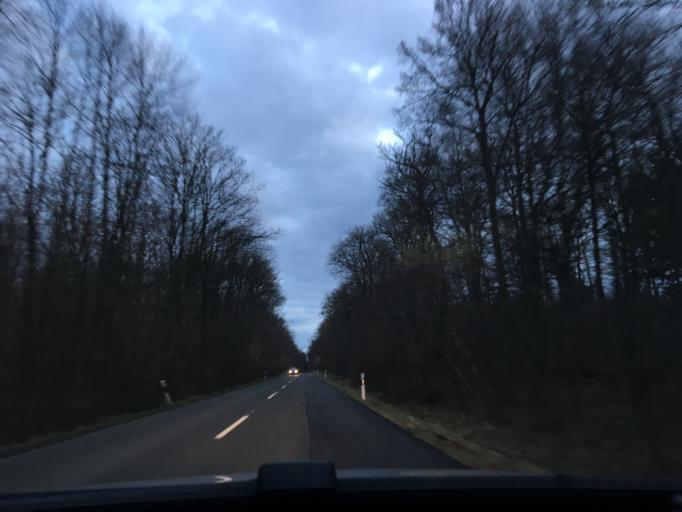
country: DE
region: Rheinland-Pfalz
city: Bechenheim
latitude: 49.7170
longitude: 8.0023
